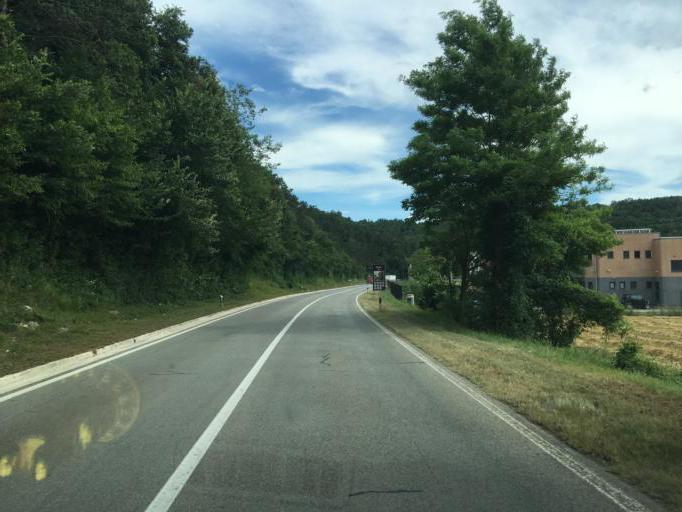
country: HR
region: Istarska
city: Pazin
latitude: 45.2488
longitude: 13.8949
